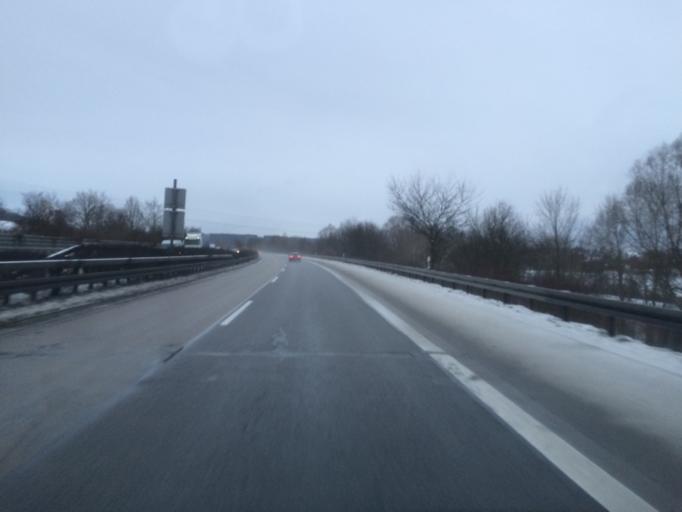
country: DE
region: Bavaria
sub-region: Upper Palatinate
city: Lappersdorf
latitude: 49.0555
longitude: 12.0928
